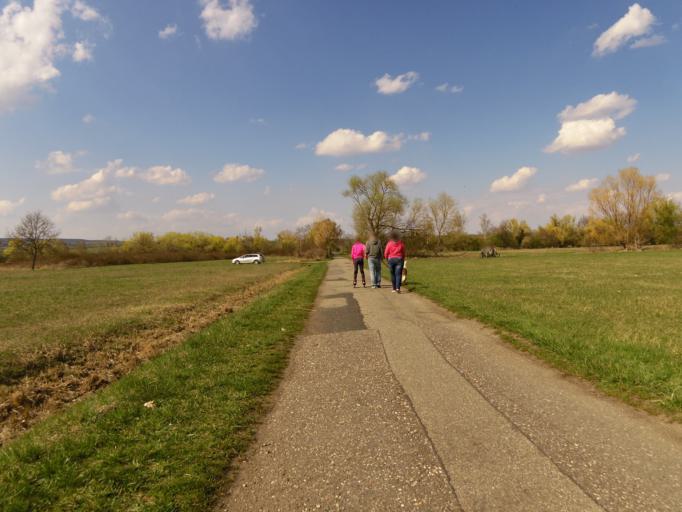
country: DE
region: Rheinland-Pfalz
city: Erpolzheim
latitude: 49.4815
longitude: 8.2038
